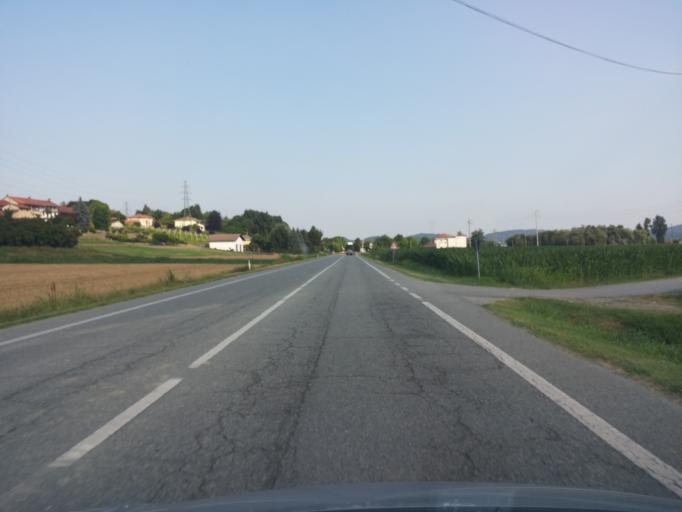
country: IT
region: Piedmont
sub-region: Provincia di Torino
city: Piverone
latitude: 45.4338
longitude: 8.0220
